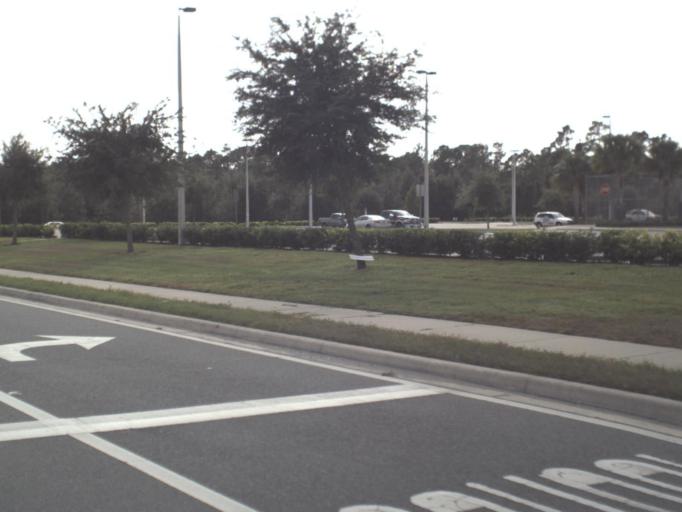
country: US
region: Florida
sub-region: Osceola County
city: Buenaventura Lakes
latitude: 28.3794
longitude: -81.2446
